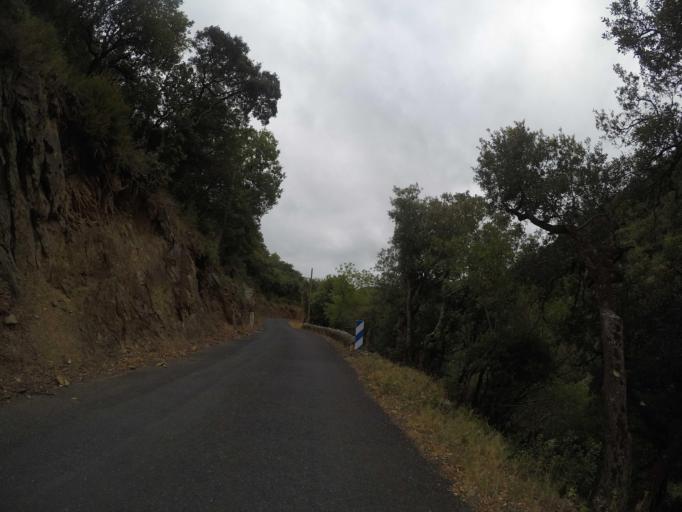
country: FR
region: Languedoc-Roussillon
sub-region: Departement des Pyrenees-Orientales
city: Ille-sur-Tet
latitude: 42.6383
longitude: 2.6206
